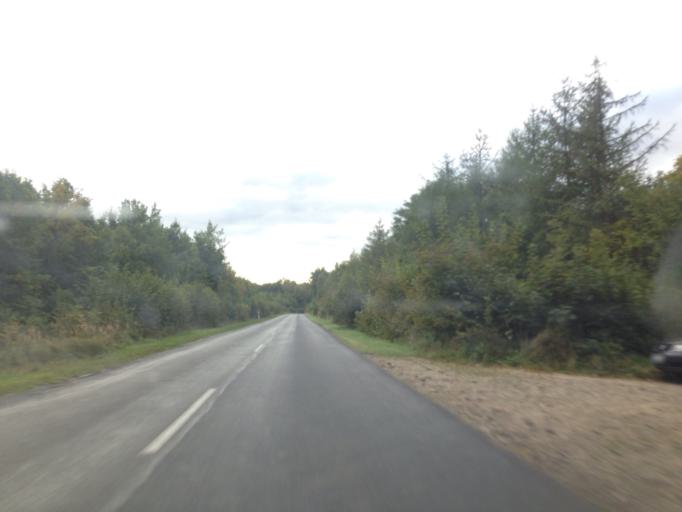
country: PL
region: Pomeranian Voivodeship
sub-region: Powiat kwidzynski
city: Prabuty
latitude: 53.7397
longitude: 19.1185
